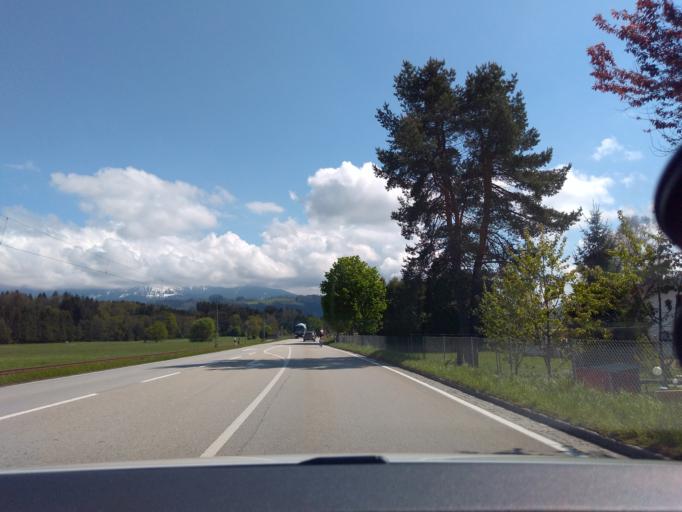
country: DE
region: Bavaria
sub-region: Upper Bavaria
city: Rohrdorf
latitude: 47.8151
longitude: 12.1590
